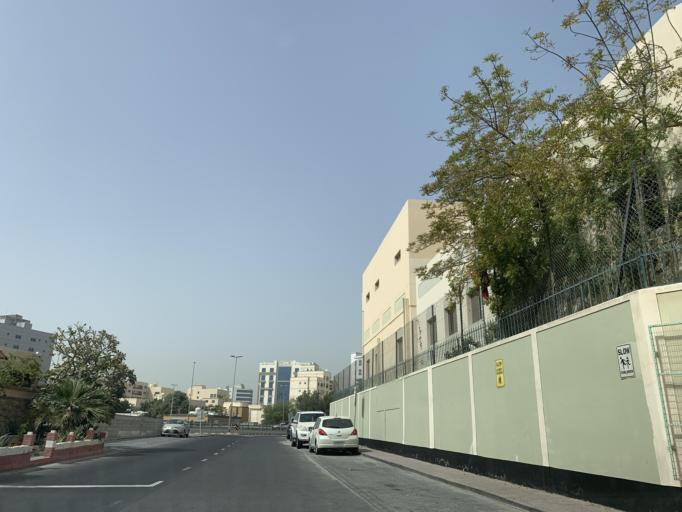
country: BH
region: Manama
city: Manama
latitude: 26.2062
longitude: 50.6007
